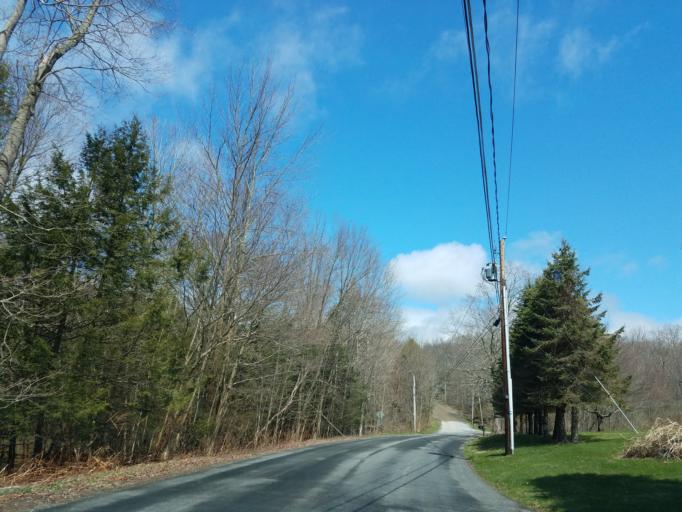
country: US
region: Connecticut
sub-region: Litchfield County
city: West Torrington
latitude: 41.7842
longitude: -73.1652
